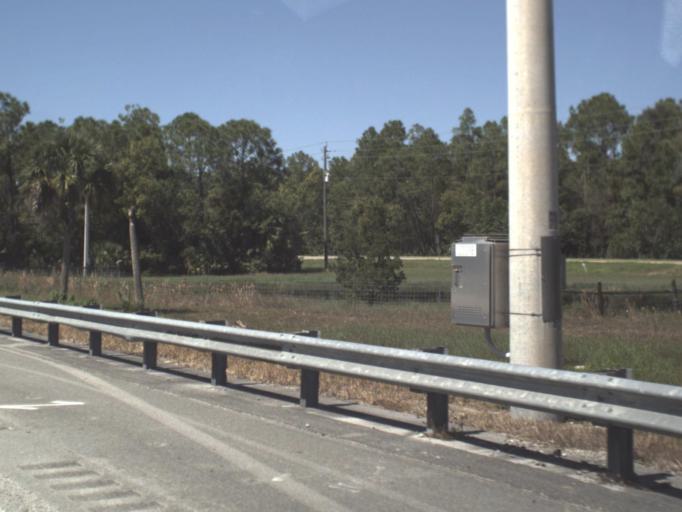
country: US
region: Florida
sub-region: Collier County
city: Golden Gate
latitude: 26.1559
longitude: -81.6689
